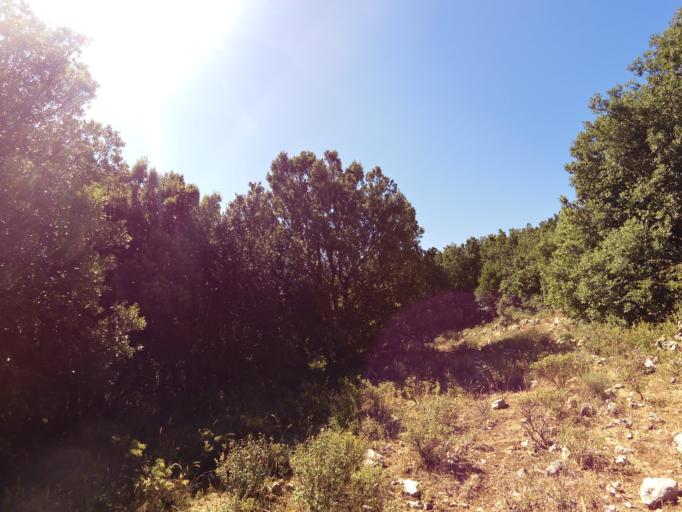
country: IT
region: Calabria
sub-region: Provincia di Reggio Calabria
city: Pazzano
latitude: 38.4615
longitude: 16.4304
